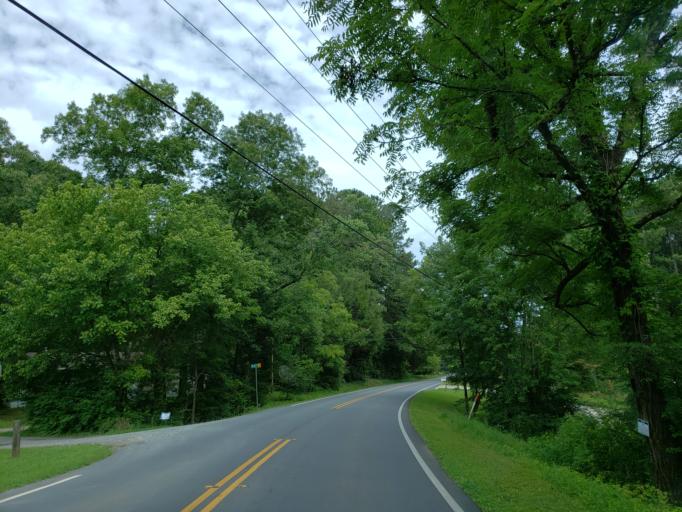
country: US
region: Georgia
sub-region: Pickens County
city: Jasper
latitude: 34.4454
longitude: -84.4132
